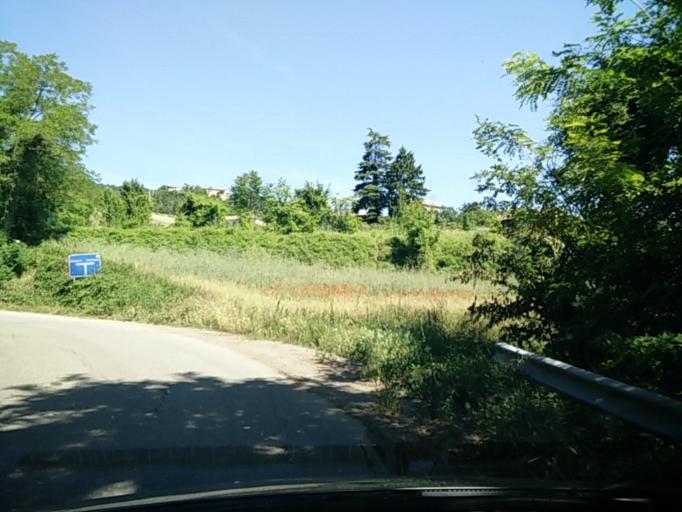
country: IT
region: Lombardy
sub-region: Provincia di Pavia
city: Susella
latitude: 44.9006
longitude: 9.1042
